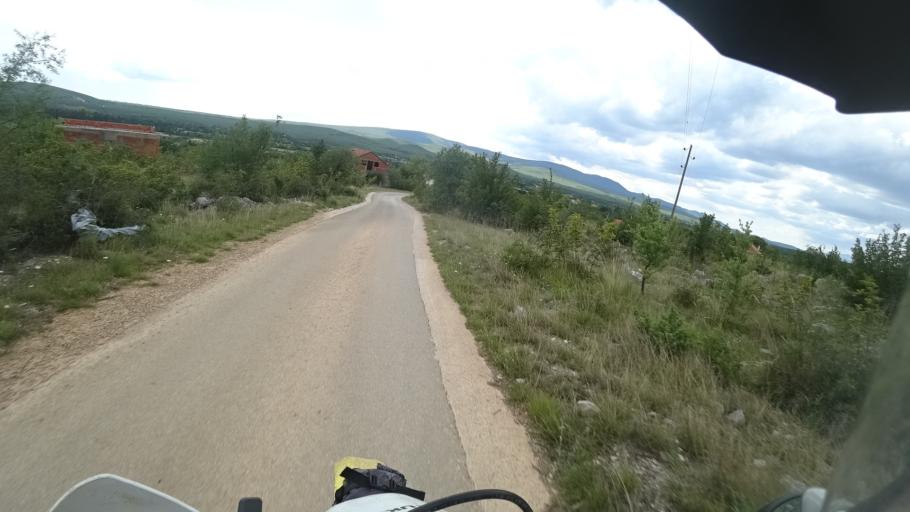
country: HR
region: Sibensko-Kniniska
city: Kistanje
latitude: 44.1075
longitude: 15.9502
